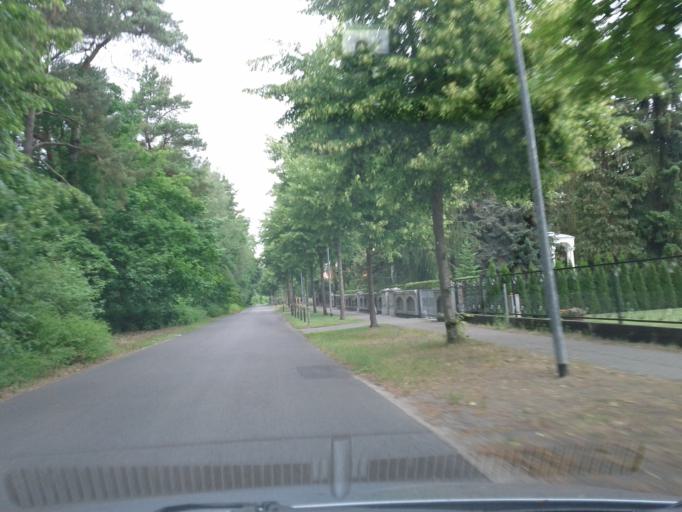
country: DE
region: Brandenburg
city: Schoneiche
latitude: 52.4640
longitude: 13.7098
